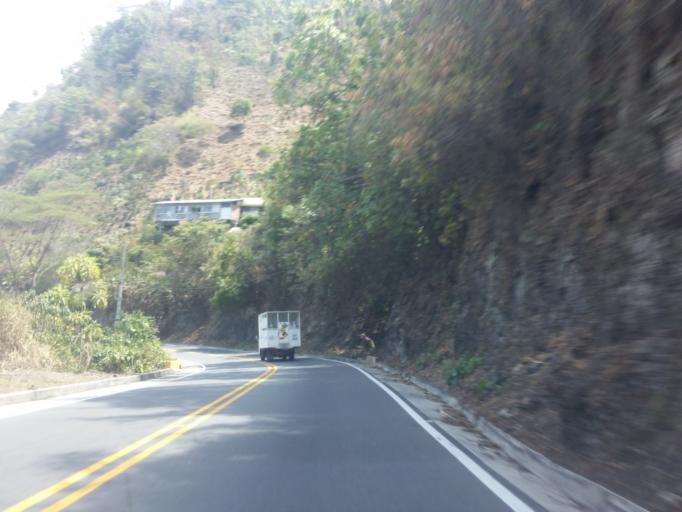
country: CO
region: Caldas
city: Chinchina
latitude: 5.0069
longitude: -75.5648
